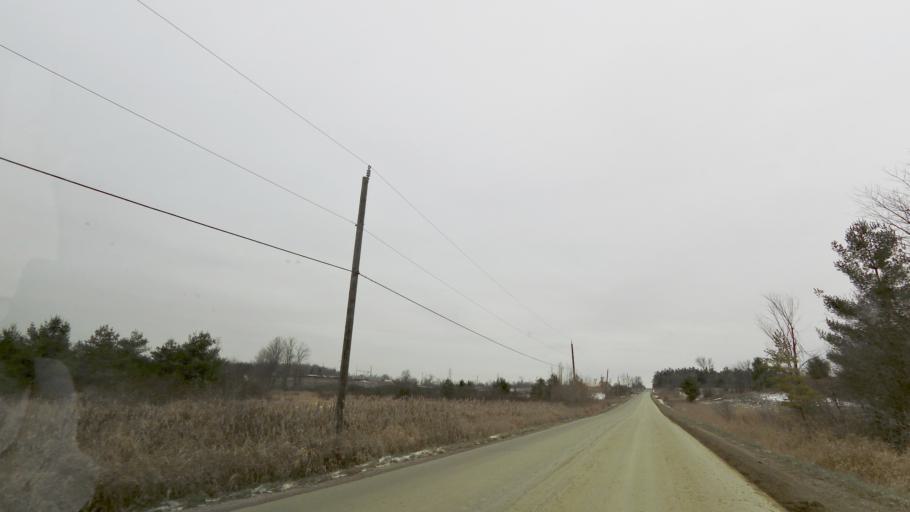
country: CA
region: Ontario
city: Vaughan
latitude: 43.8670
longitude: -79.6178
